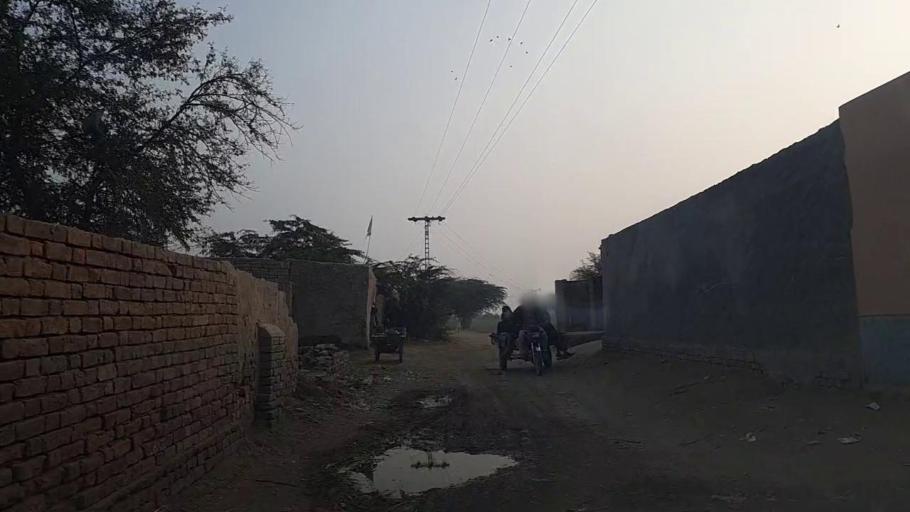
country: PK
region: Sindh
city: Sinjhoro
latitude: 26.1036
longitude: 68.7968
